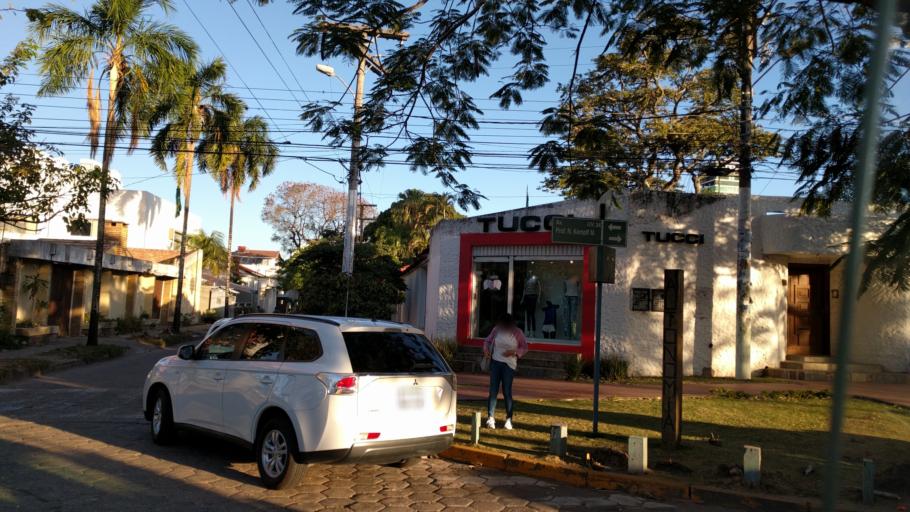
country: BO
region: Santa Cruz
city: Santa Cruz de la Sierra
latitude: -17.7636
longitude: -63.1940
